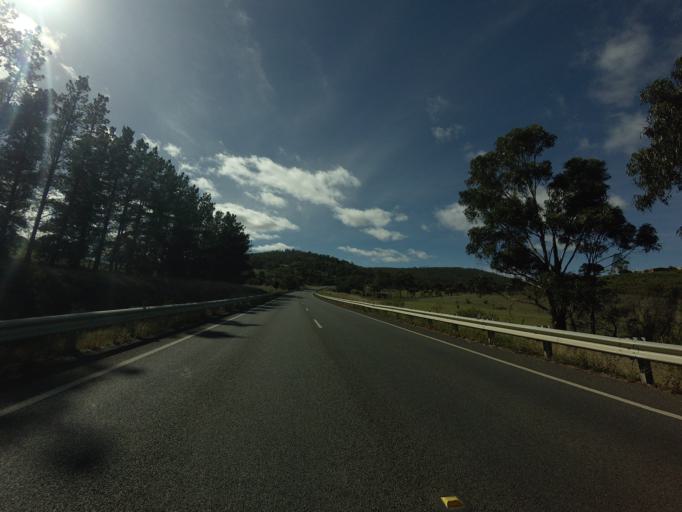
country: AU
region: Tasmania
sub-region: Sorell
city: Sorell
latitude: -42.7824
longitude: 147.5953
